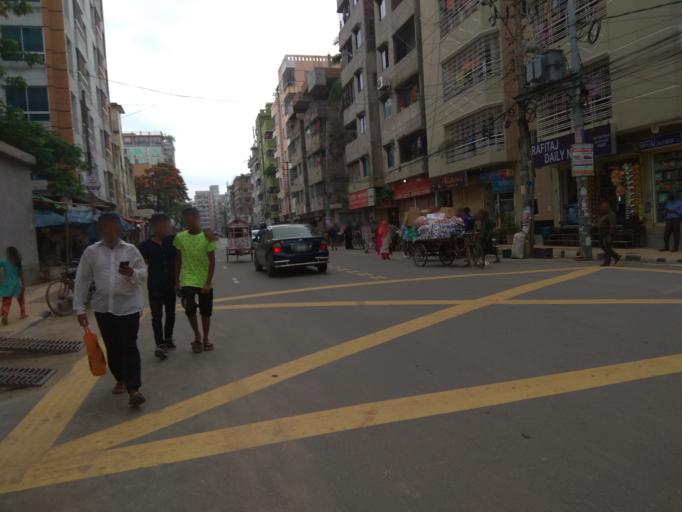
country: BD
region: Dhaka
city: Azimpur
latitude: 23.8075
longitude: 90.3754
